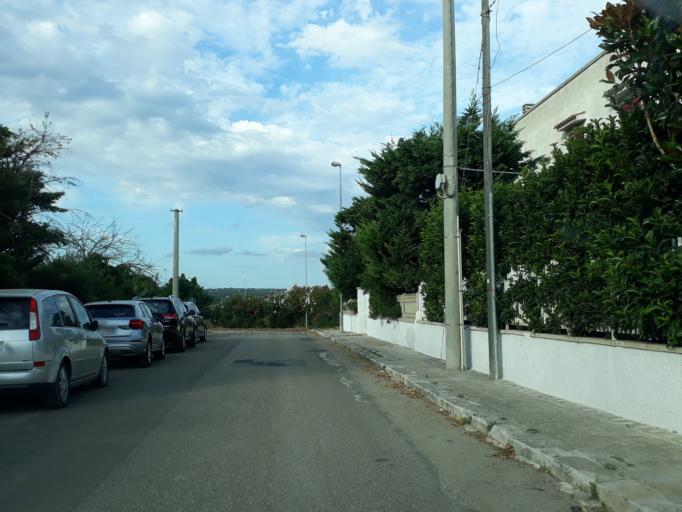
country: IT
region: Apulia
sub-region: Provincia di Brindisi
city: Carovigno
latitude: 40.7555
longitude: 17.6973
